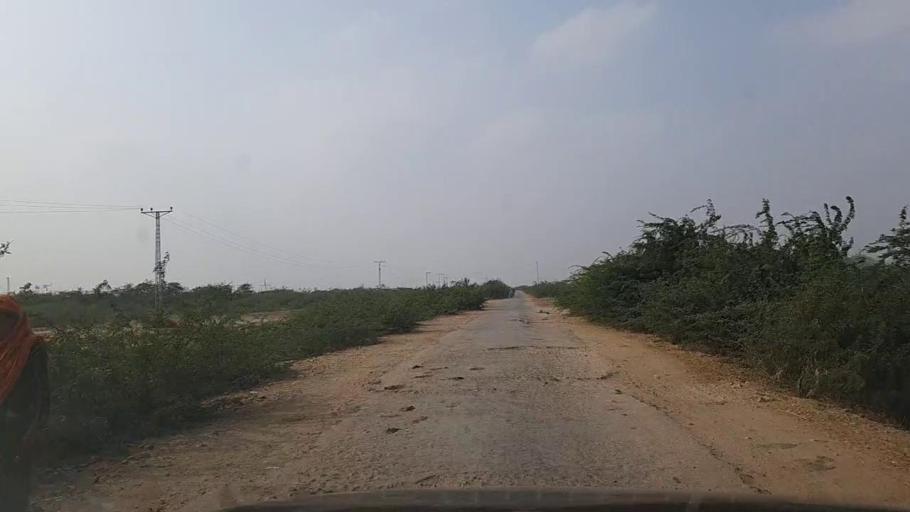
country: PK
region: Sindh
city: Thatta
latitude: 24.8585
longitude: 67.7766
